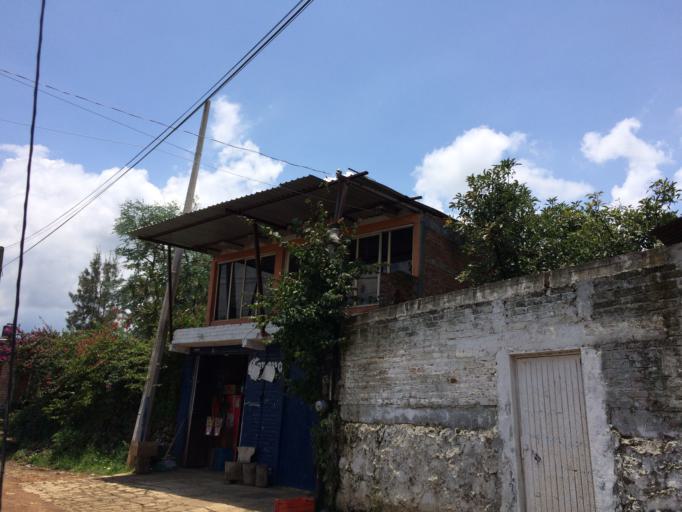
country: MX
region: Michoacan
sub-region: Periban
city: San Francisco Periban
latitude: 19.5574
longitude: -102.3960
